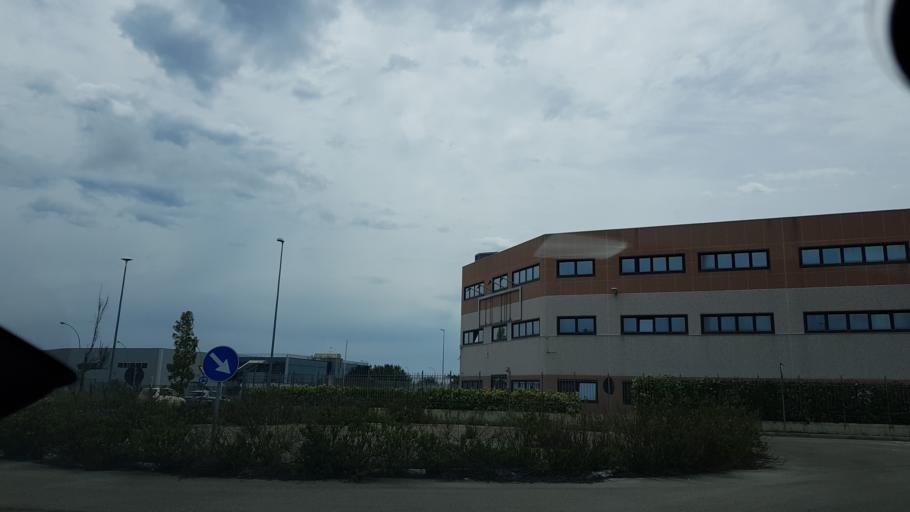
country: IT
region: Apulia
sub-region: Provincia di Brindisi
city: Materdomini
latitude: 40.6339
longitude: 17.9581
